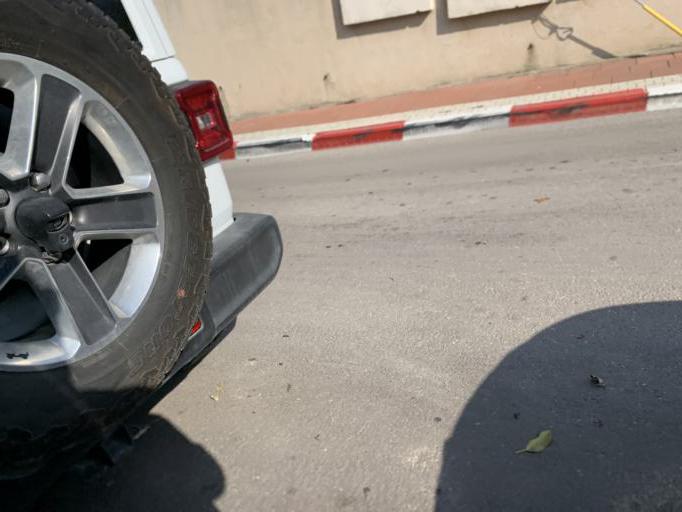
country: IL
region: Tel Aviv
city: Ramat Gan
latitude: 32.0946
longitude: 34.8179
